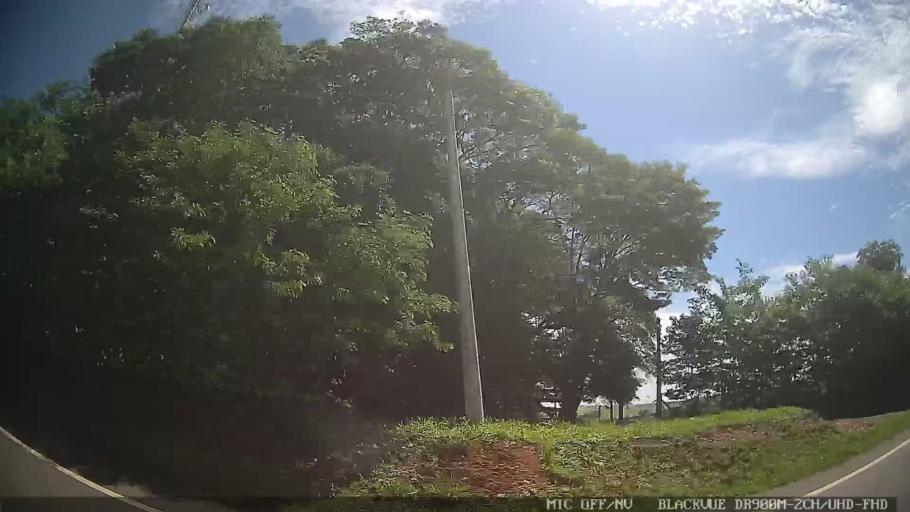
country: BR
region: Sao Paulo
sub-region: Tiete
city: Tiete
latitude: -23.1567
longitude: -47.6569
